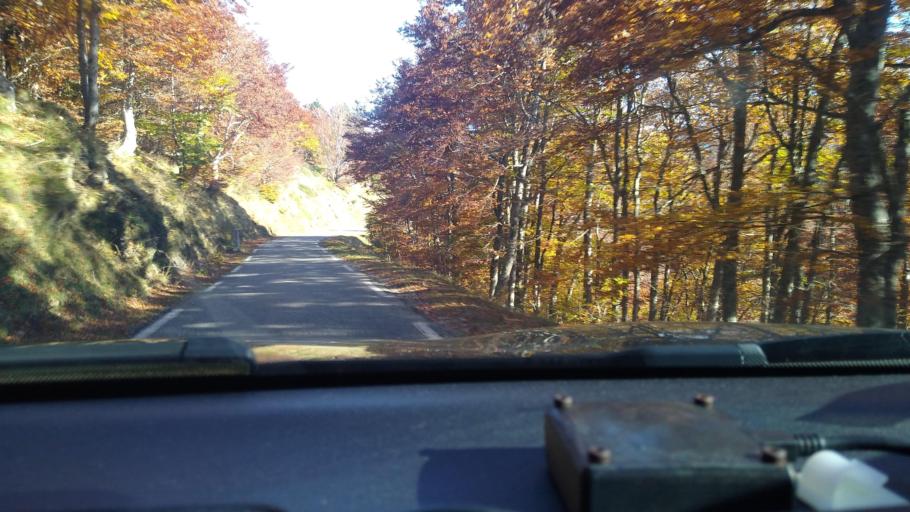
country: FR
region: Midi-Pyrenees
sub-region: Departement de l'Ariege
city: Ax-les-Thermes
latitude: 42.7301
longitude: 2.0025
